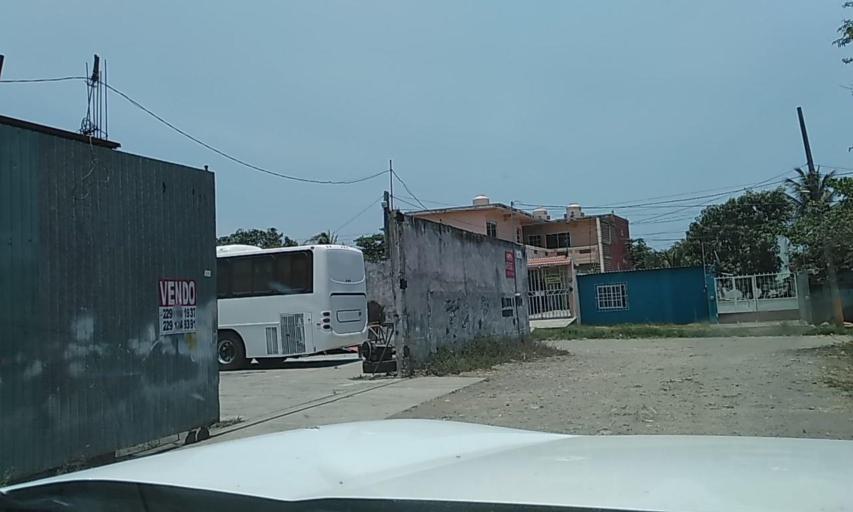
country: MX
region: Veracruz
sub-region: Veracruz
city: Las Amapolas
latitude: 19.1533
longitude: -96.1997
